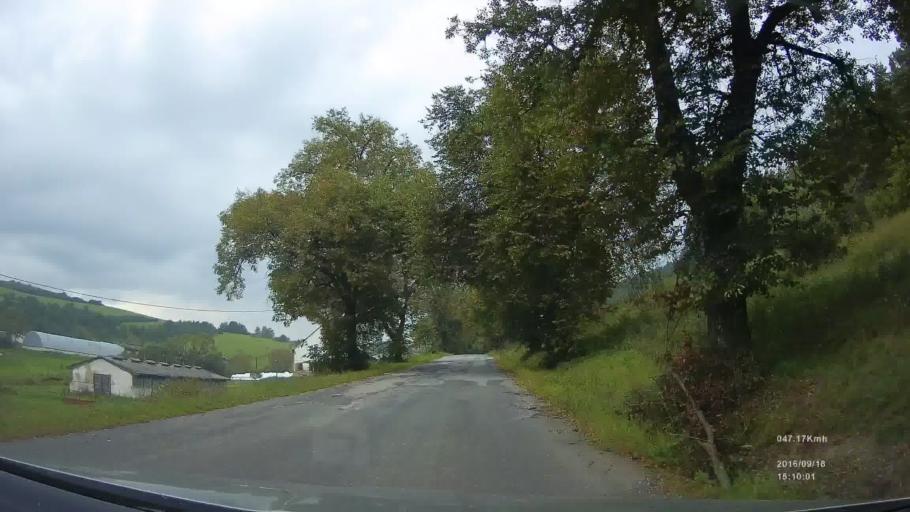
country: SK
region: Presovsky
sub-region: Okres Presov
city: Levoca
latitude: 49.0181
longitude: 20.5042
